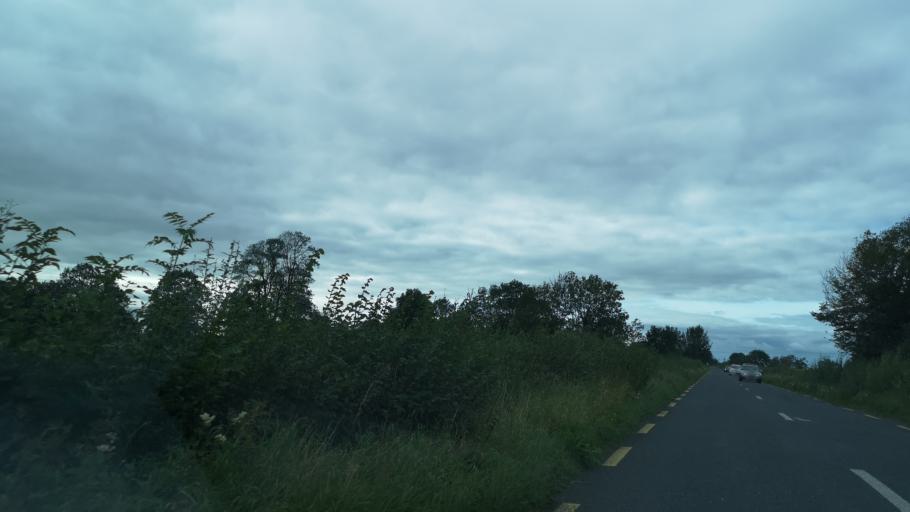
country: IE
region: Leinster
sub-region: Uibh Fhaili
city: Banagher
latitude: 53.2558
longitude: -7.9580
